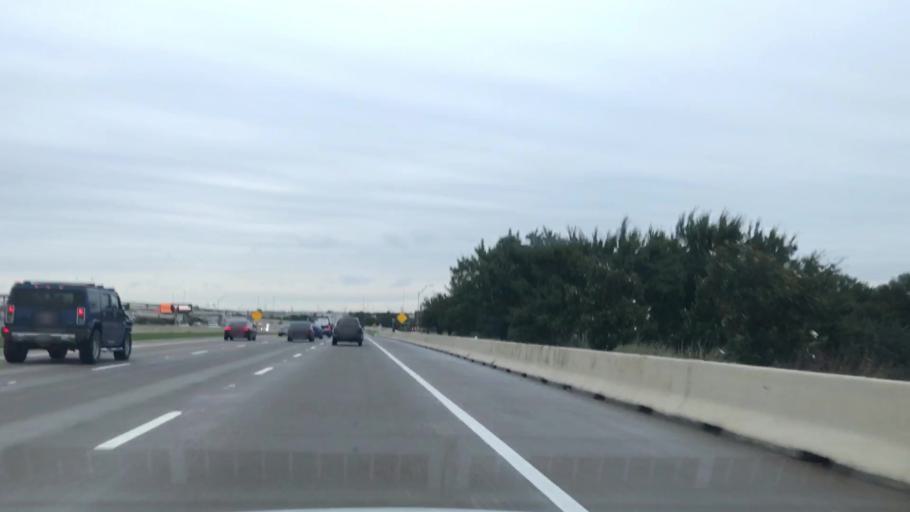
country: US
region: Texas
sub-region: Denton County
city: Lewisville
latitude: 32.9939
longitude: -96.9726
